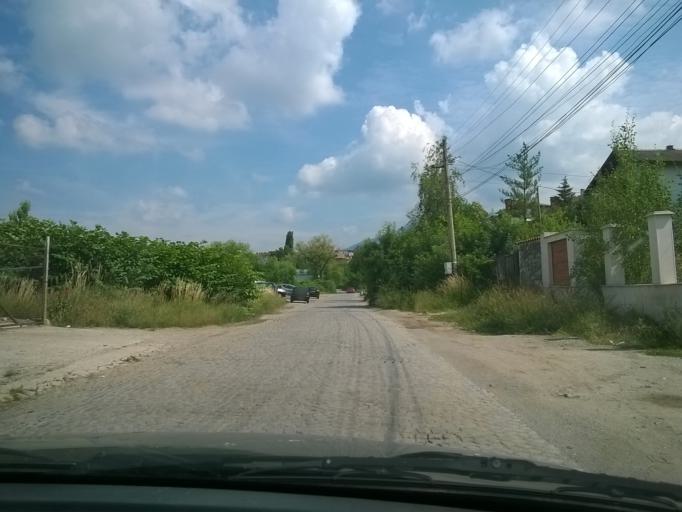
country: BG
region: Sofiya
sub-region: Obshtina Bozhurishte
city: Bozhurishte
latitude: 42.6844
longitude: 23.2361
